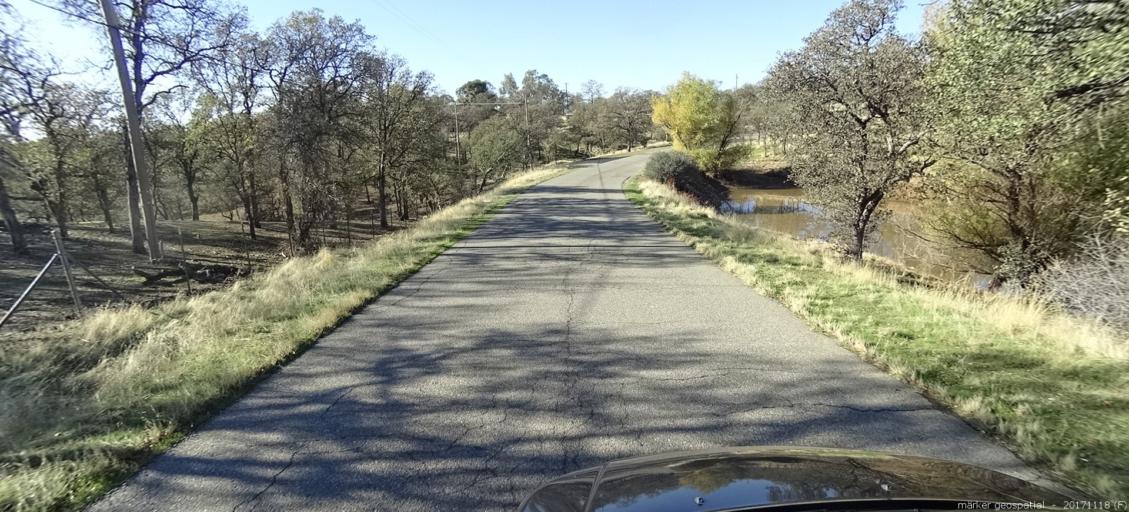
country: US
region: California
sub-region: Shasta County
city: Cottonwood
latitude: 40.3947
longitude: -122.3210
